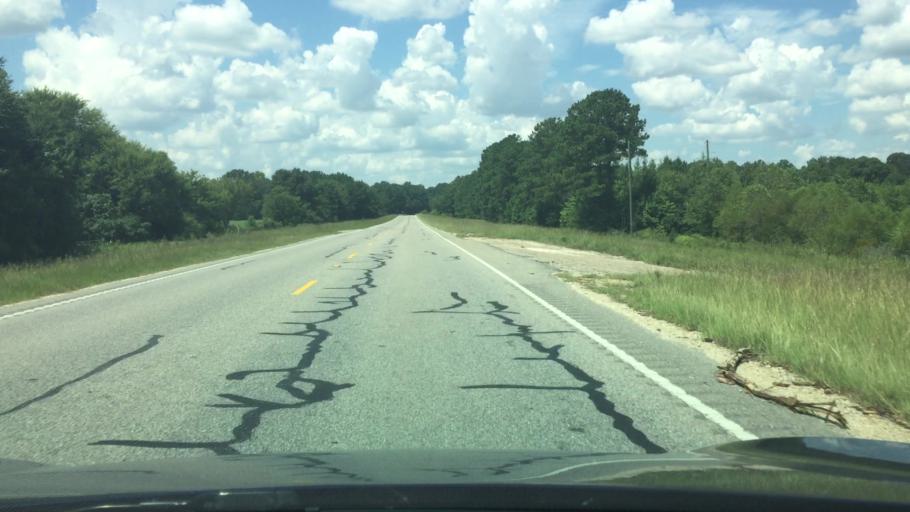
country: US
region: Alabama
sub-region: Montgomery County
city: Pike Road
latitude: 32.3721
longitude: -86.0081
